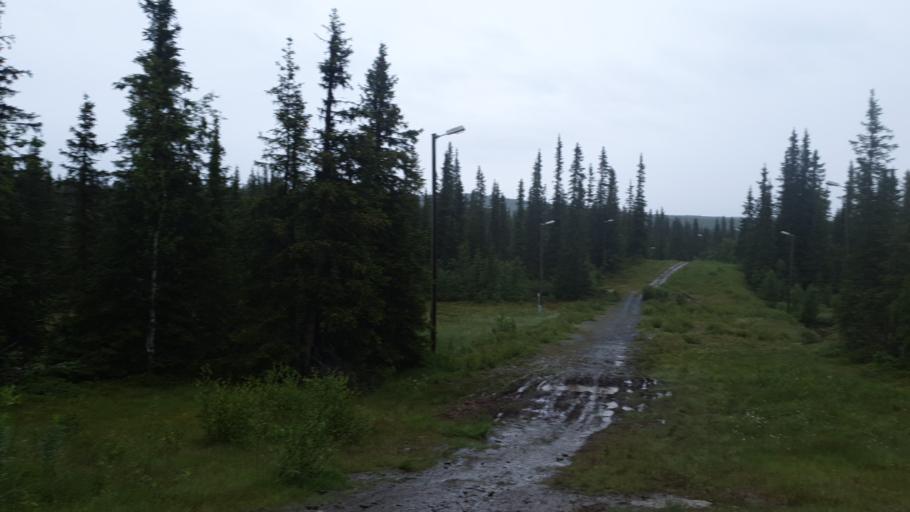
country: NO
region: Oppland
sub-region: Vestre Slidre
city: Slidre
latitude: 61.2320
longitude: 8.9125
